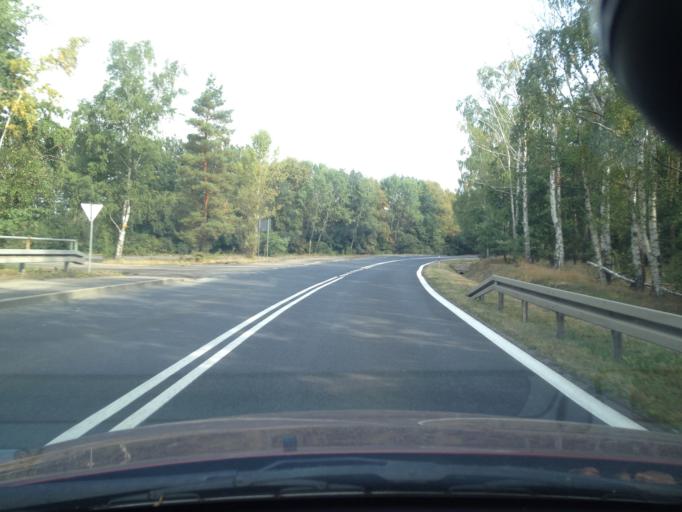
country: PL
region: Lubusz
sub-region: Powiat zaganski
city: Szprotawa
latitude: 51.4435
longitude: 15.5995
